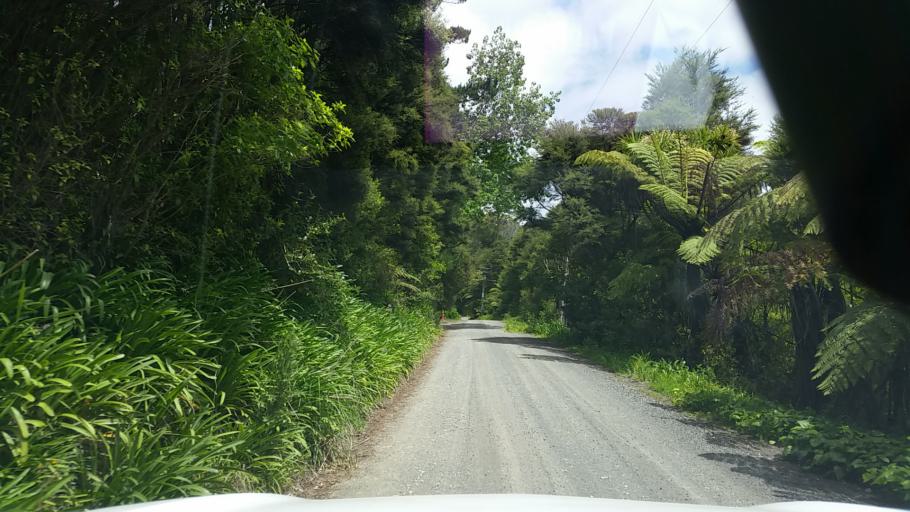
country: NZ
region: Auckland
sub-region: Auckland
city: Rosebank
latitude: -36.8531
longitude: 174.5879
